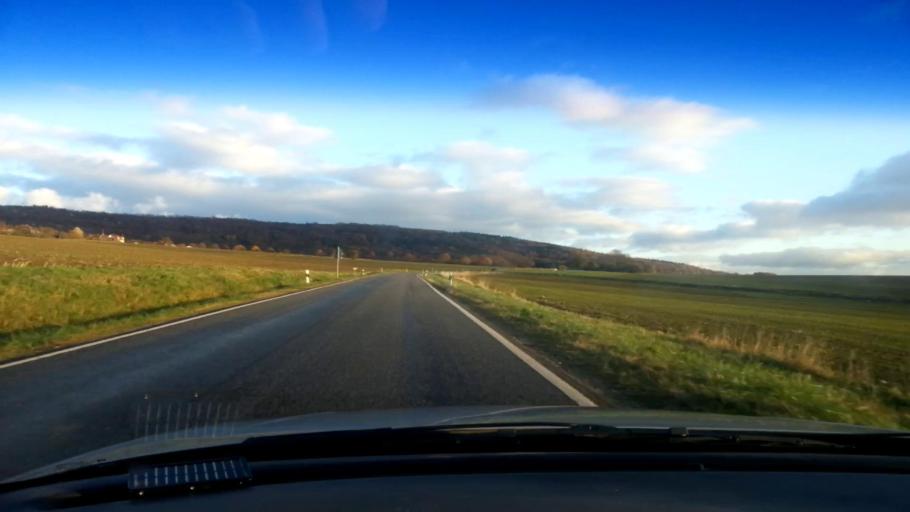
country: DE
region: Bavaria
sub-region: Upper Franconia
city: Buttenheim
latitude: 49.8424
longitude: 11.0237
